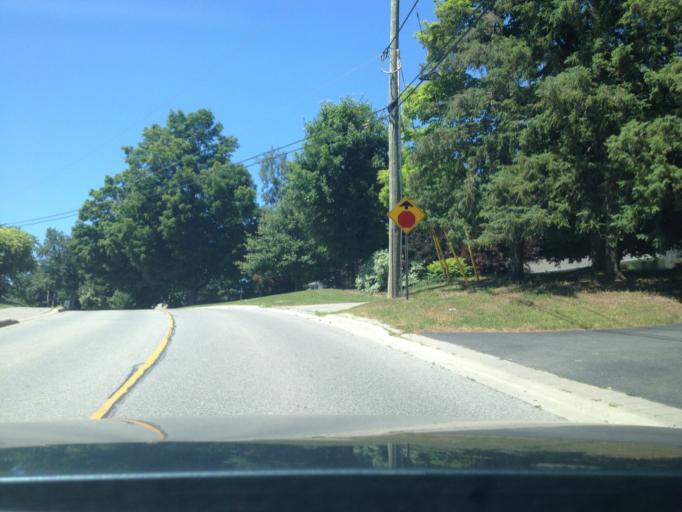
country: CA
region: Ontario
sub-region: Halton
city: Milton
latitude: 43.6628
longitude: -79.9326
